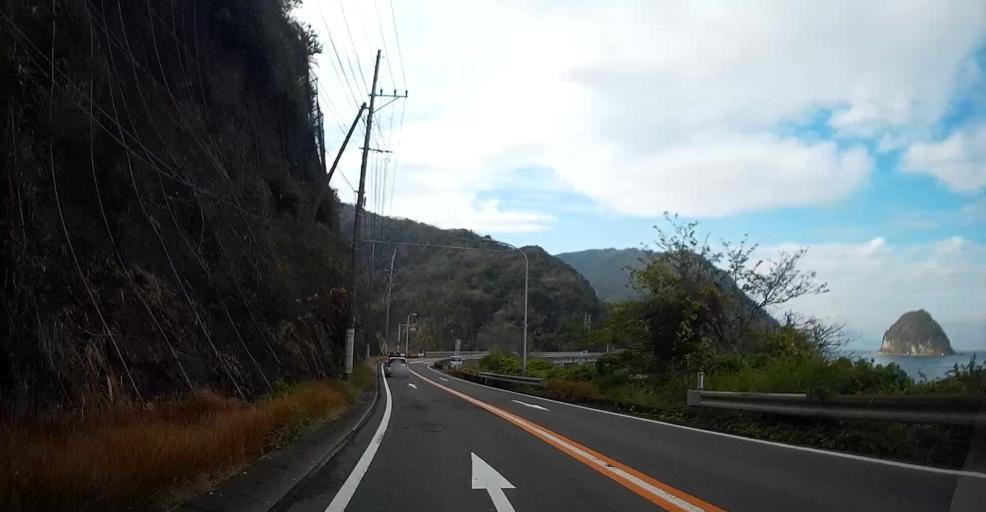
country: JP
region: Kumamoto
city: Yatsushiro
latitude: 32.6156
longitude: 130.4535
